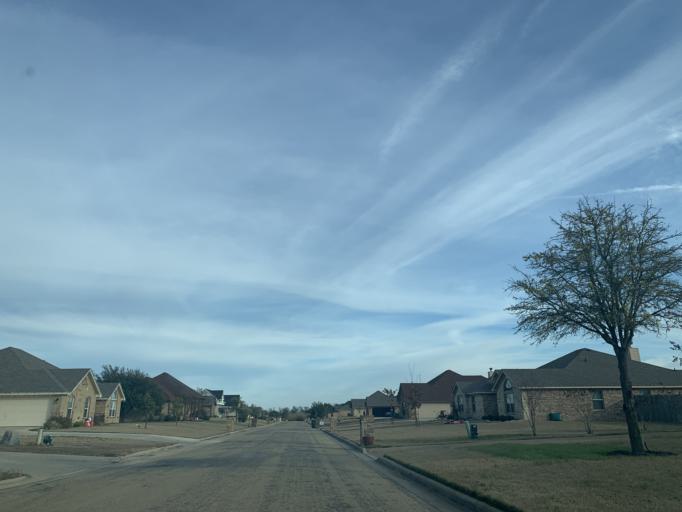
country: US
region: Texas
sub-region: Bell County
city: Salado
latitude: 30.9703
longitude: -97.5137
